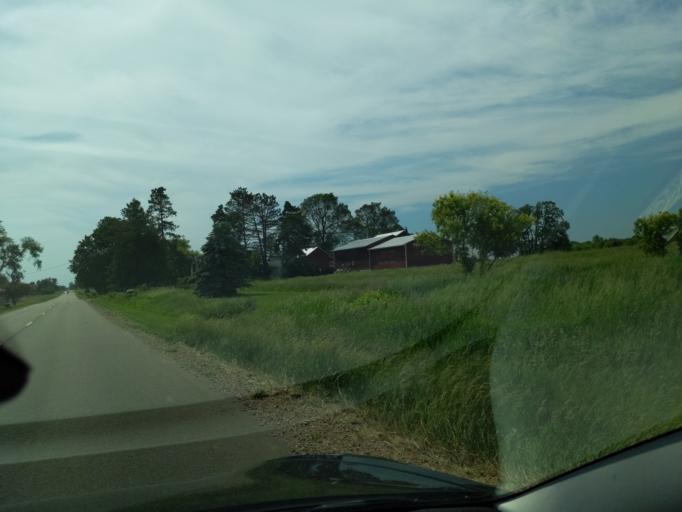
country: US
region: Michigan
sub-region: Eaton County
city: Grand Ledge
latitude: 42.7120
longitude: -84.8616
